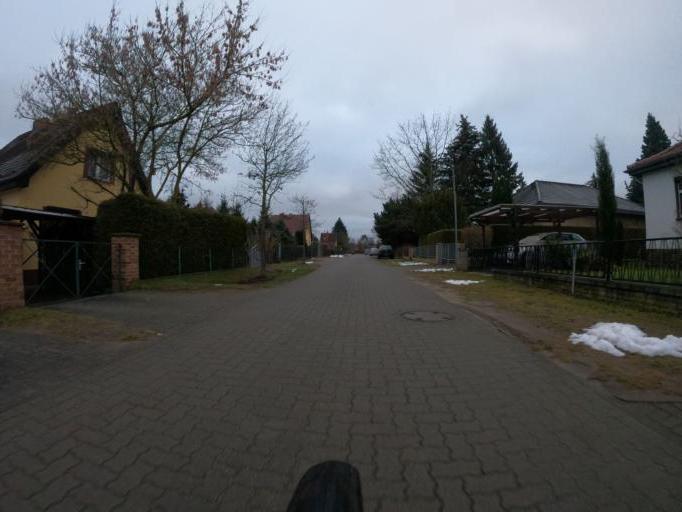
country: DE
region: Brandenburg
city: Schulzendorf
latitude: 52.3617
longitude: 13.5944
